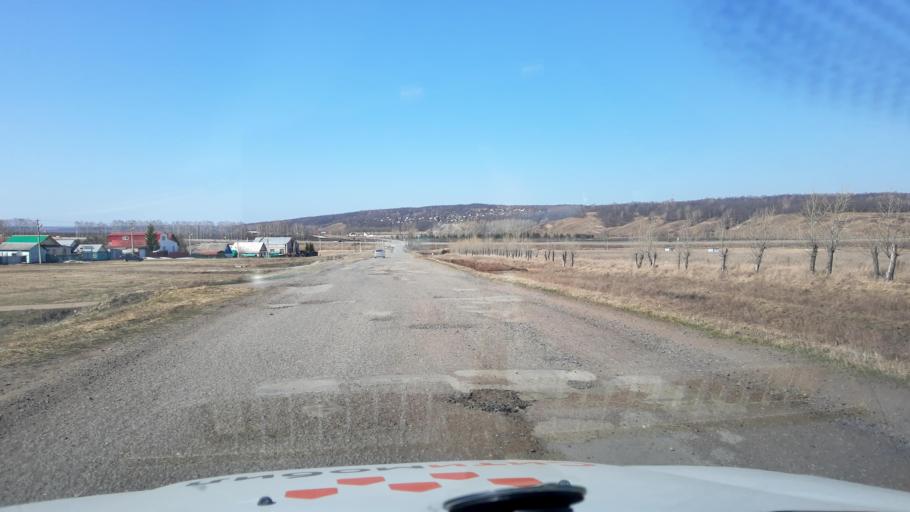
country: RU
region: Bashkortostan
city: Karmaskaly
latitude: 54.3558
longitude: 55.9234
